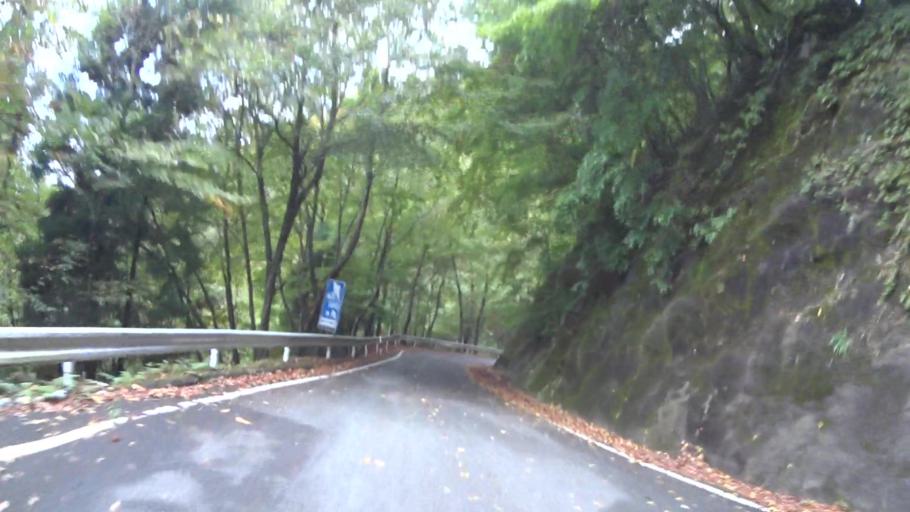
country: JP
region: Shiga Prefecture
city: Kitahama
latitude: 35.2768
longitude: 135.7282
